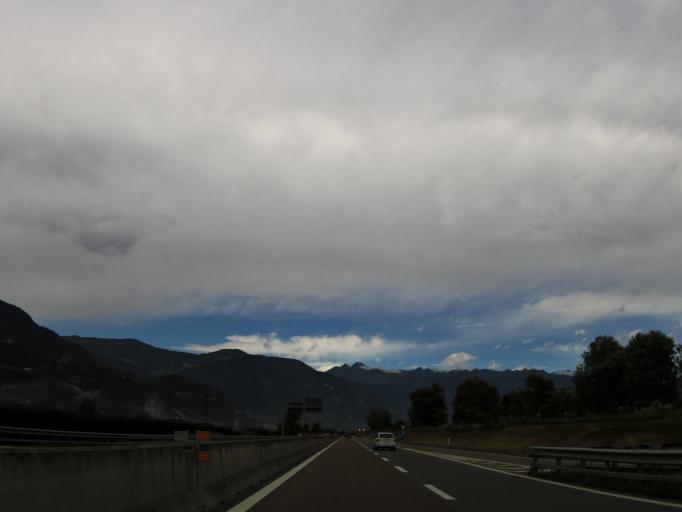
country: IT
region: Trentino-Alto Adige
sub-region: Bolzano
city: Gargazzone
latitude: 46.5774
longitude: 11.1942
